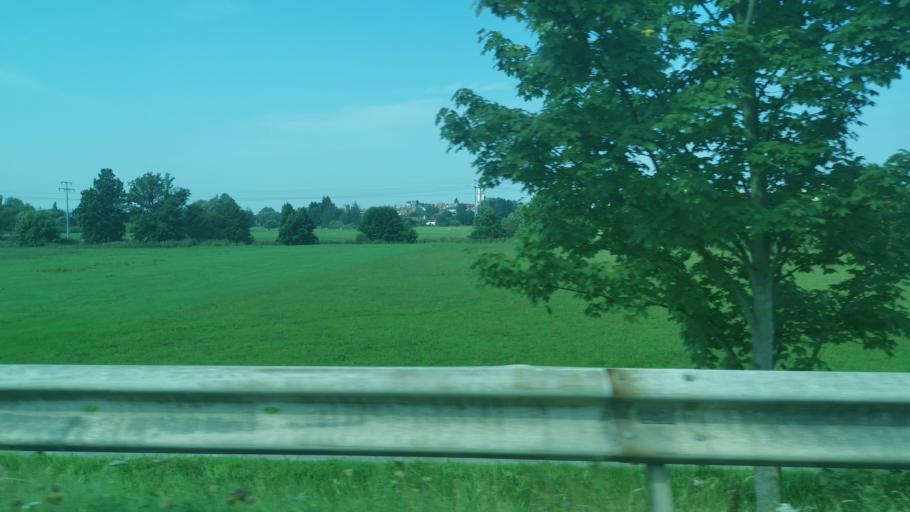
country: DE
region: Bavaria
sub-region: Upper Palatinate
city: Cham
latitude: 49.2180
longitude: 12.6793
